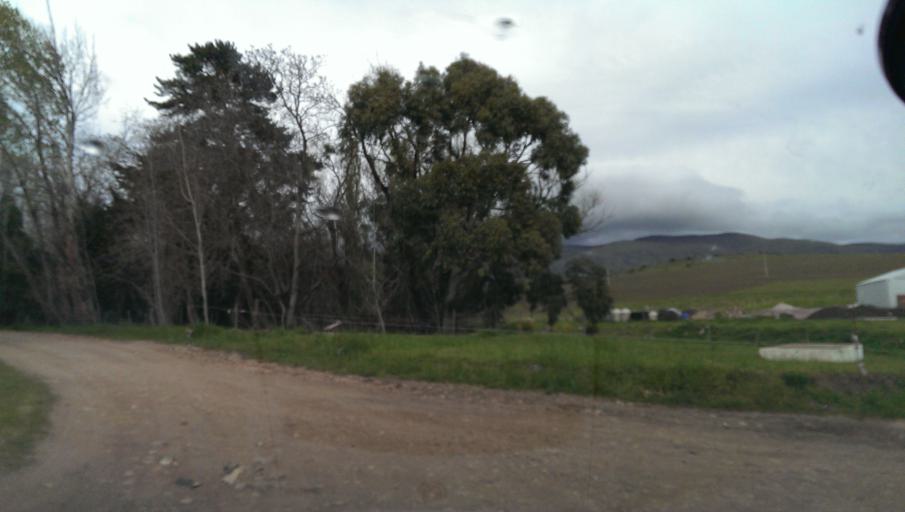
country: AR
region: Buenos Aires
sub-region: Partido de Tornquist
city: Tornquist
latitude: -38.0744
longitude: -61.9278
